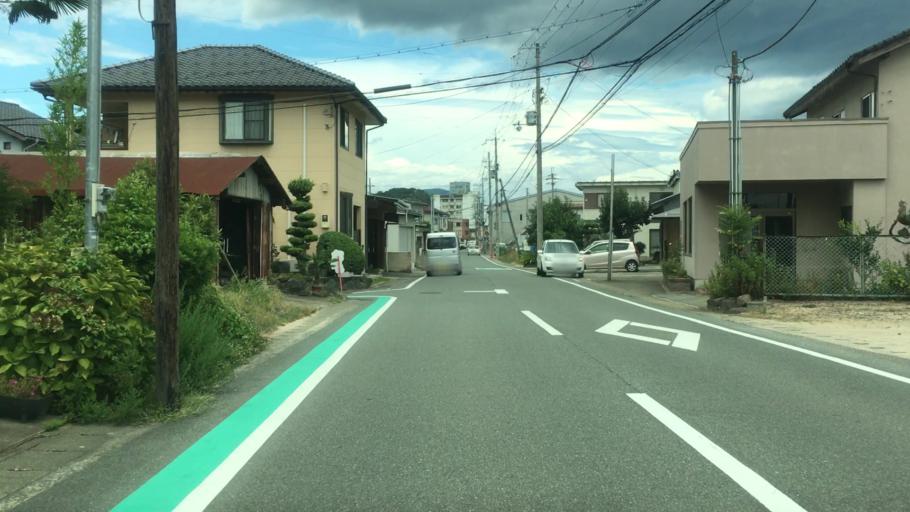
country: JP
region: Hyogo
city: Toyooka
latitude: 35.5292
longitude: 134.8221
